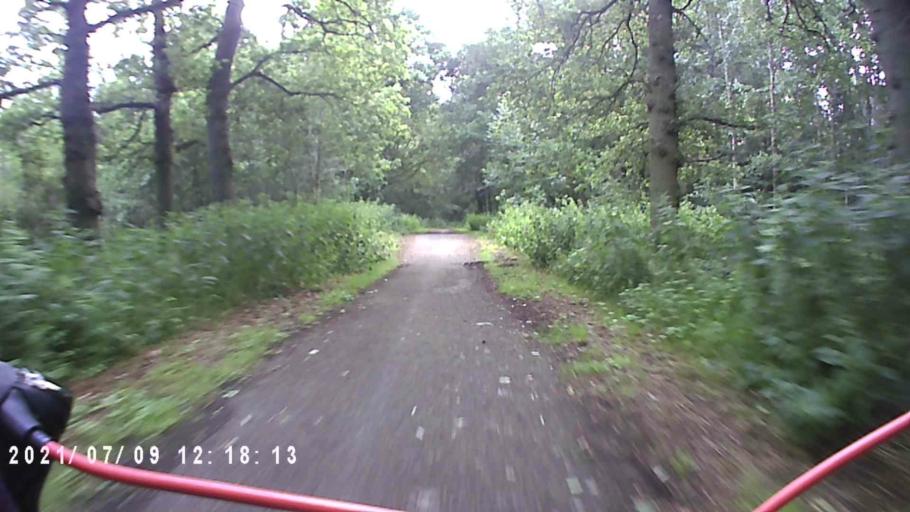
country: NL
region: Groningen
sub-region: Gemeente  Oldambt
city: Winschoten
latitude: 53.1757
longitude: 7.0032
